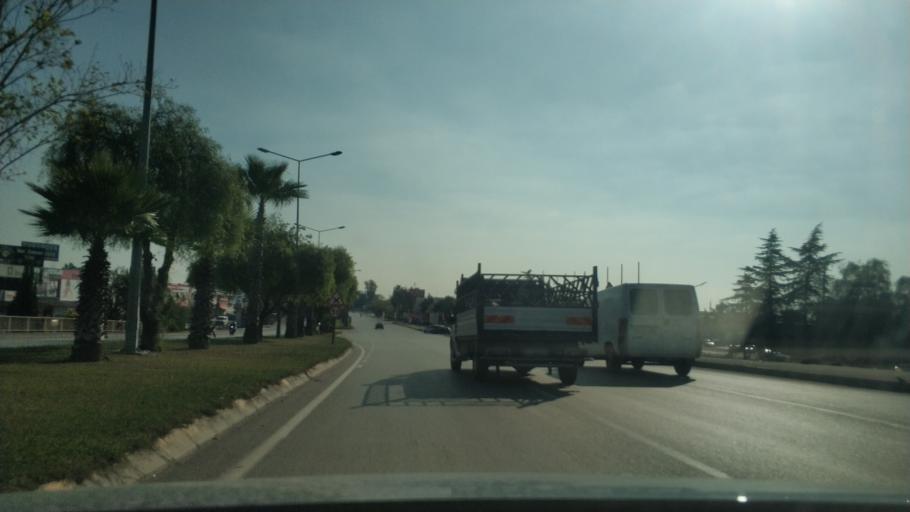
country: TR
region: Adana
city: Seyhan
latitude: 36.9958
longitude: 35.2522
